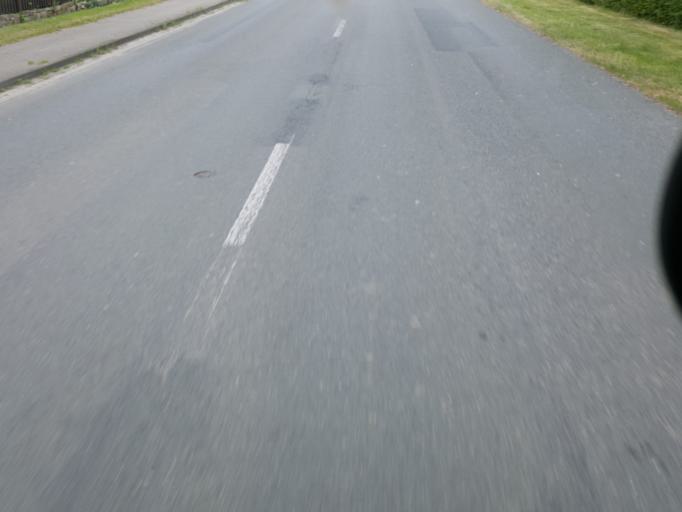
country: DE
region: Lower Saxony
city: Wolpinghausen
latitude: 52.4511
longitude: 9.2539
